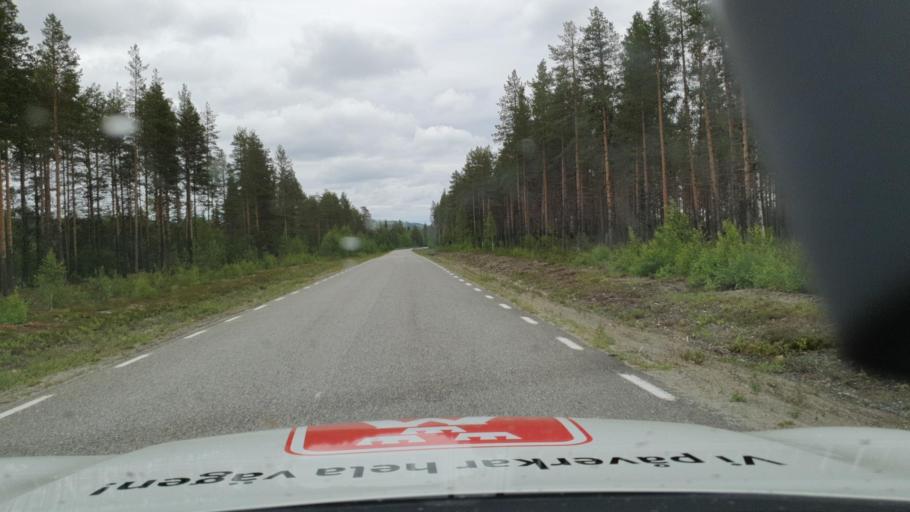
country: SE
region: Vaesterbotten
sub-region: Lycksele Kommun
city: Lycksele
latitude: 64.2116
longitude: 18.2700
